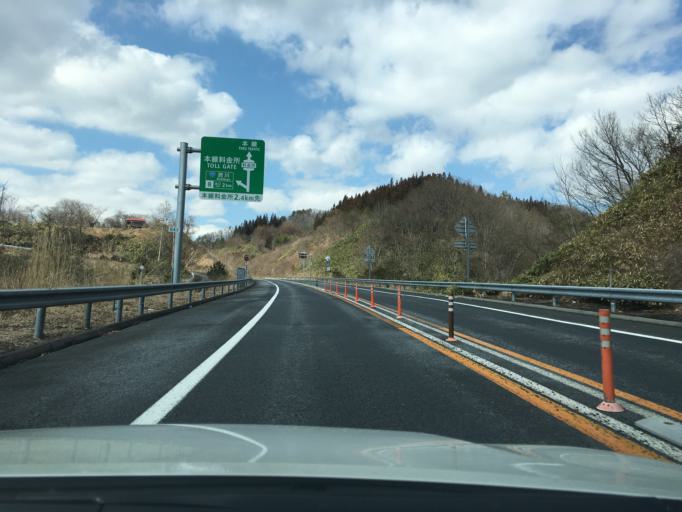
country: JP
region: Yamagata
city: Sagae
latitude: 38.4167
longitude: 140.1882
